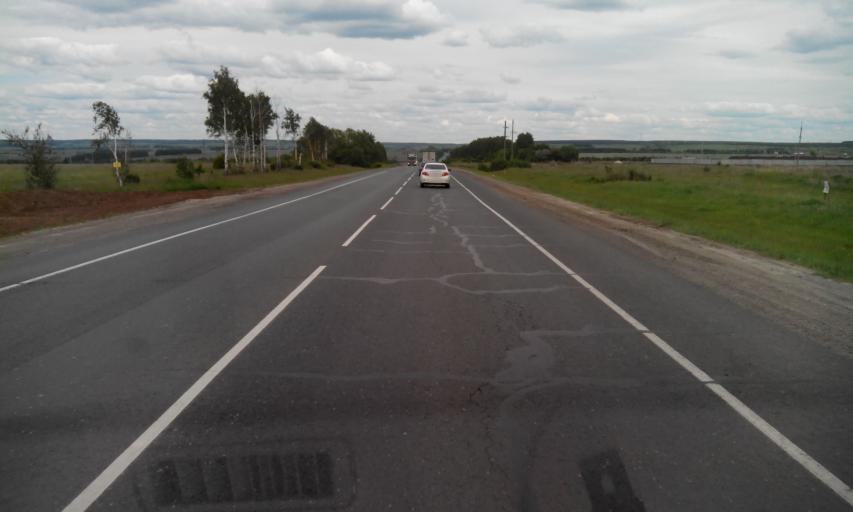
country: RU
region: Penza
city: Chemodanovka
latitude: 53.2200
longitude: 45.3119
